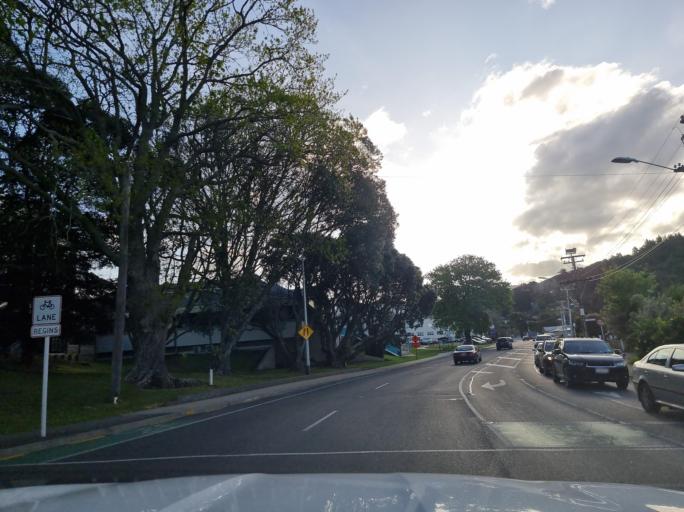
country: NZ
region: Northland
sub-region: Whangarei
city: Whangarei
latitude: -35.7345
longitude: 174.3040
